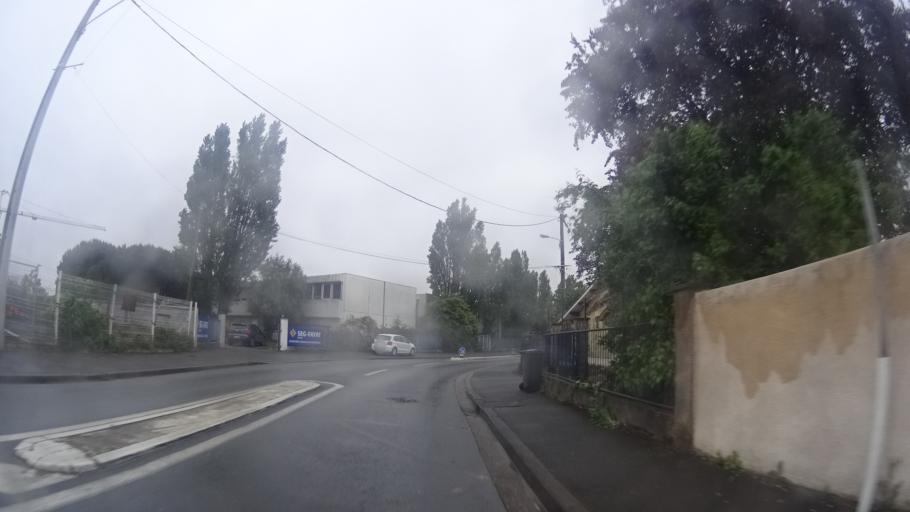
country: FR
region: Aquitaine
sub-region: Departement de la Gironde
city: Begles
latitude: 44.8343
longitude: -0.5423
